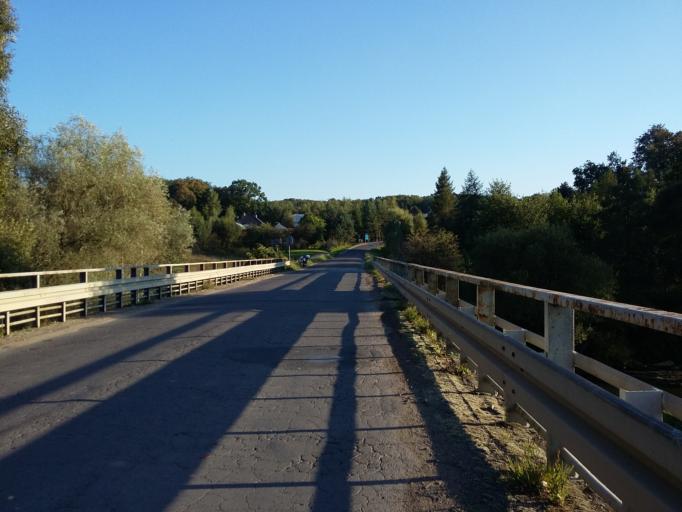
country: PL
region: Subcarpathian Voivodeship
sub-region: Powiat jasielski
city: Tarnowiec
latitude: 49.7465
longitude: 21.5901
